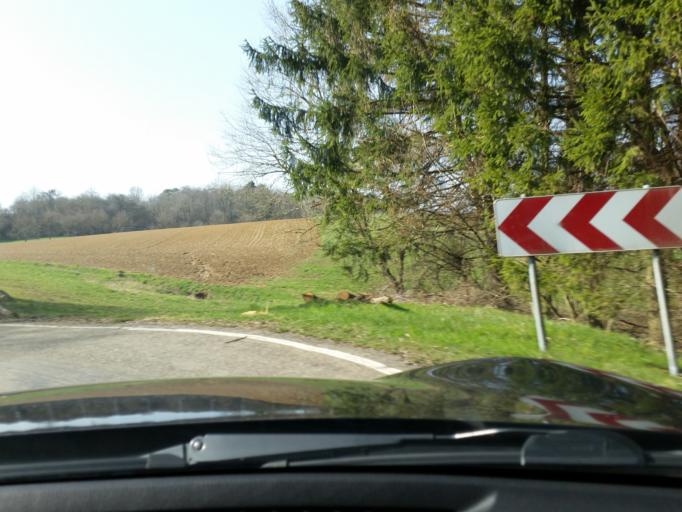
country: DE
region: Baden-Wuerttemberg
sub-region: Regierungsbezirk Stuttgart
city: Jagsthausen
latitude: 49.3618
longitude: 9.4648
